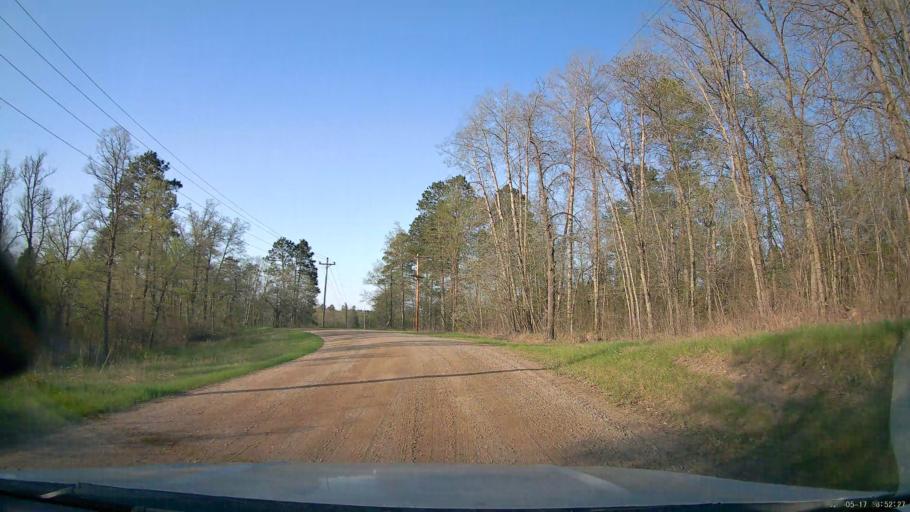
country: US
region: Minnesota
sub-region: Hubbard County
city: Park Rapids
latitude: 46.9437
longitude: -95.0010
